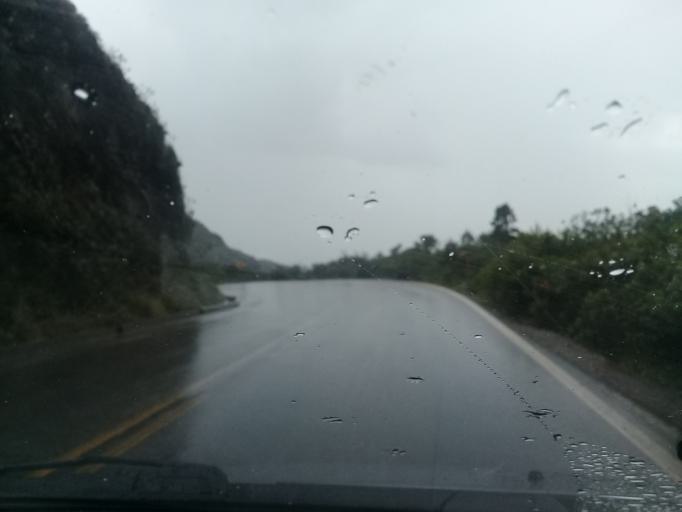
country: CO
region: Cundinamarca
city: Guasca
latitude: 4.8433
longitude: -73.8154
